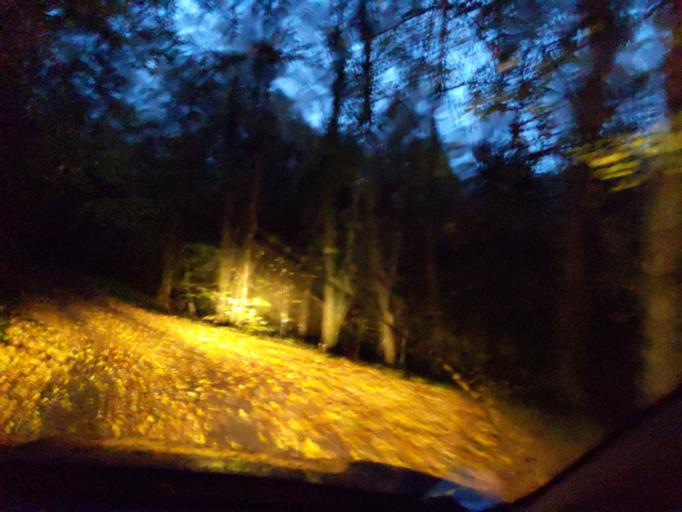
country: FR
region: Rhone-Alpes
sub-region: Departement de la Savoie
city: Aiton
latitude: 45.5161
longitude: 6.3364
